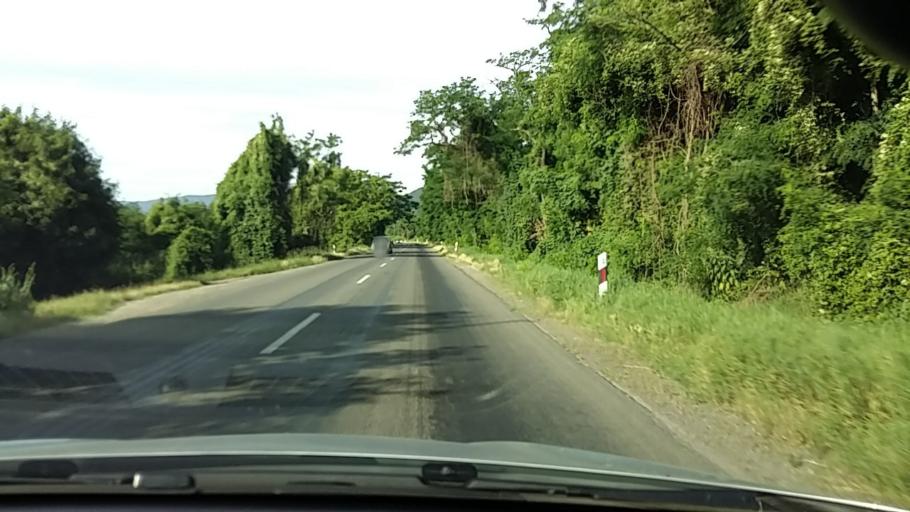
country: HU
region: Pest
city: Nagymaros
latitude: 47.8071
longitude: 18.9685
